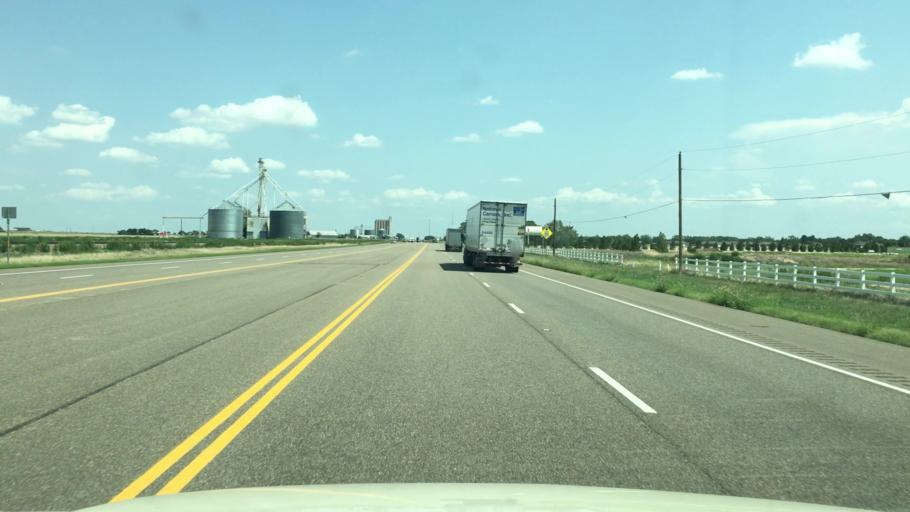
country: US
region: Texas
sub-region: Armstrong County
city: Claude
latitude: 35.1185
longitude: -101.3789
